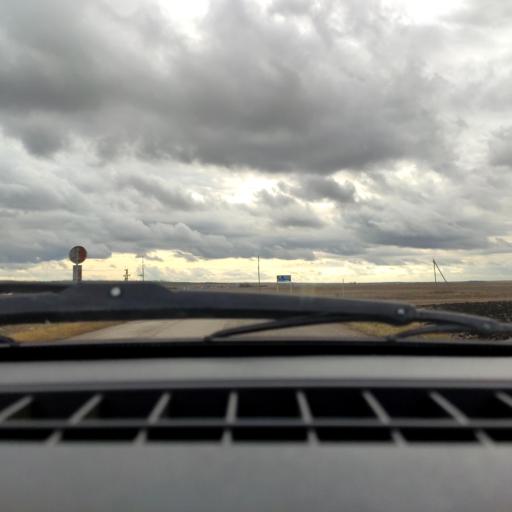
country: RU
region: Bashkortostan
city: Asanovo
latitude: 54.9392
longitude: 55.5171
